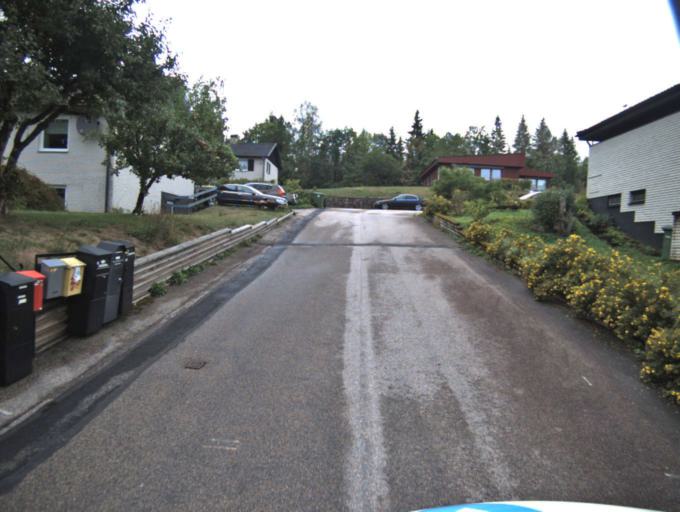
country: SE
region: Vaestra Goetaland
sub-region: Tranemo Kommun
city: Langhem
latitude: 57.7009
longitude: 13.3038
